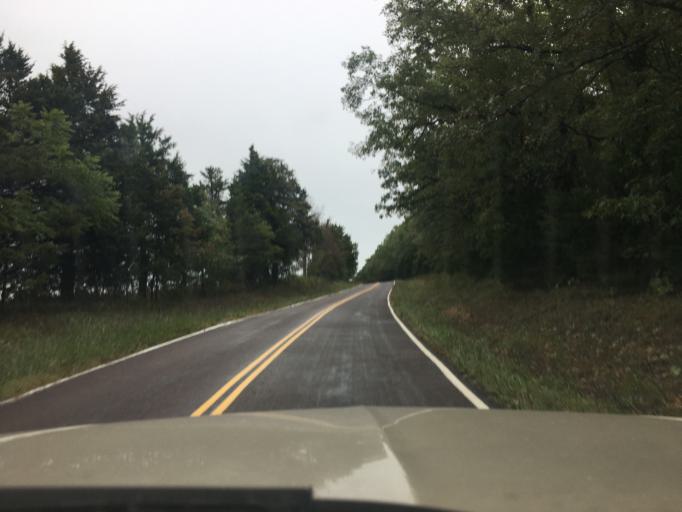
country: US
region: Missouri
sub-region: Crawford County
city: Cuba
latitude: 38.1822
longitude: -91.4879
